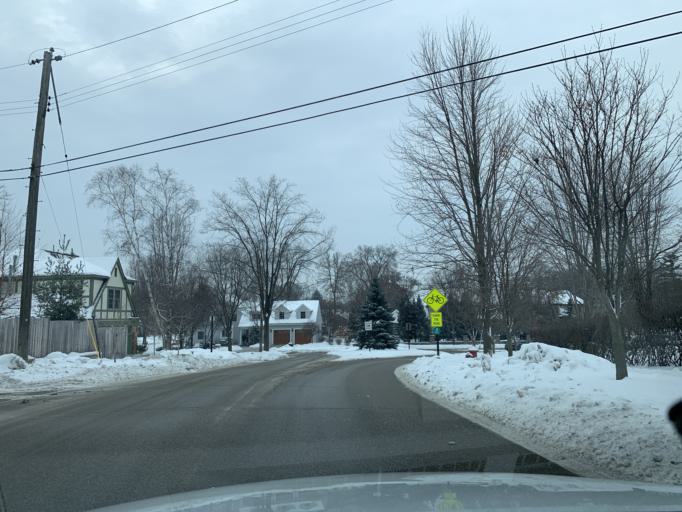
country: US
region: Minnesota
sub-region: Hennepin County
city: Saint Louis Park
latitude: 44.9200
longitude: -93.3392
